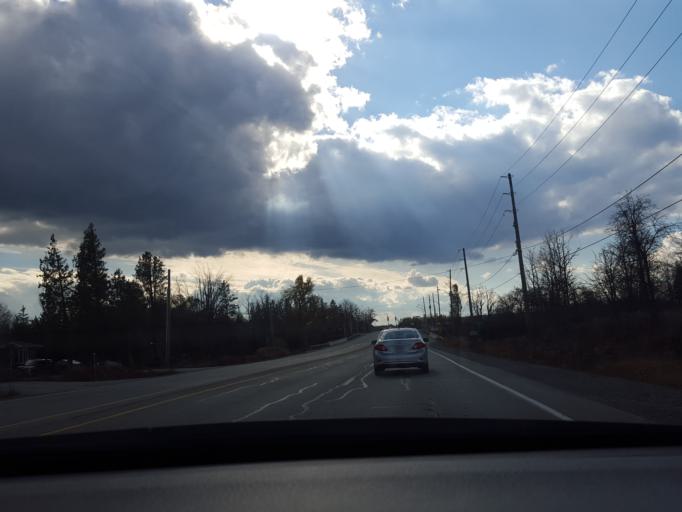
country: CA
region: Ontario
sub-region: Halton
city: Milton
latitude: 43.5471
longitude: -79.8173
